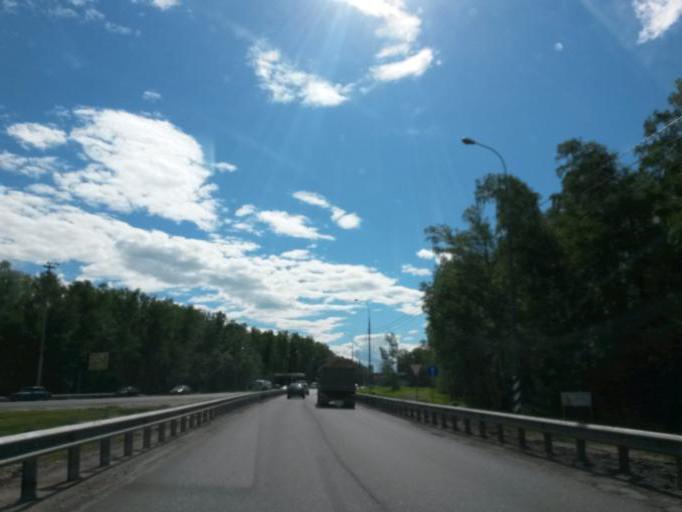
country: RU
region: Moskovskaya
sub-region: Podol'skiy Rayon
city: Podol'sk
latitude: 55.4038
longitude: 37.6013
